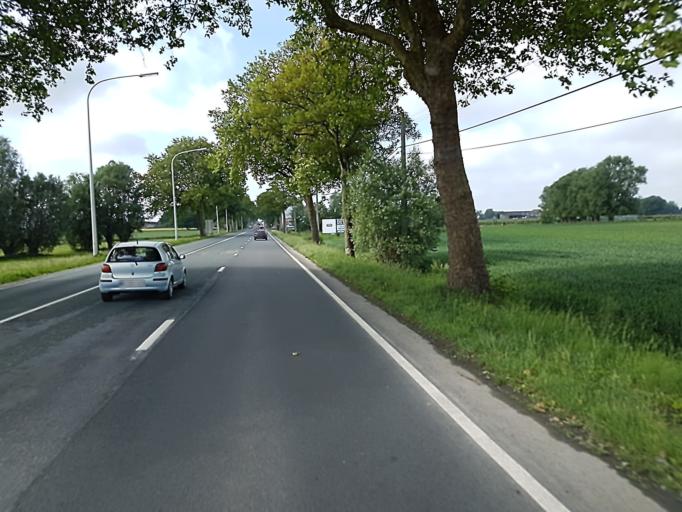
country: BE
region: Wallonia
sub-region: Province du Hainaut
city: Soignies
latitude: 50.5595
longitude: 4.0576
